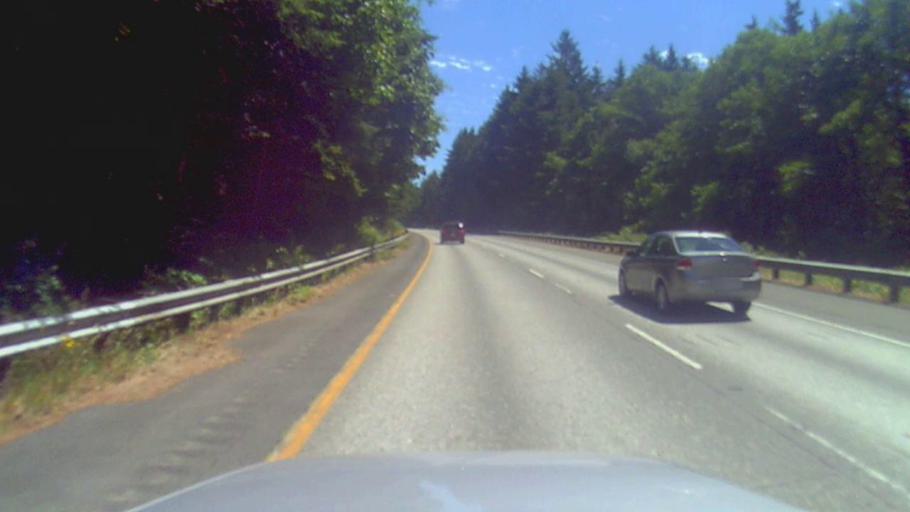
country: US
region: Washington
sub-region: Whatcom County
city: Bellingham
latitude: 48.6992
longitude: -122.4672
